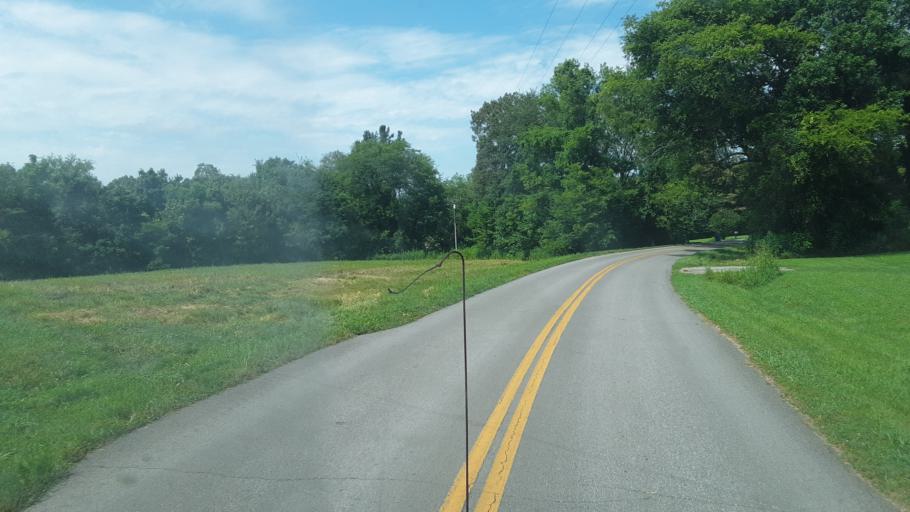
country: US
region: Kentucky
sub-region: Christian County
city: Oak Grove
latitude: 36.7312
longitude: -87.3231
